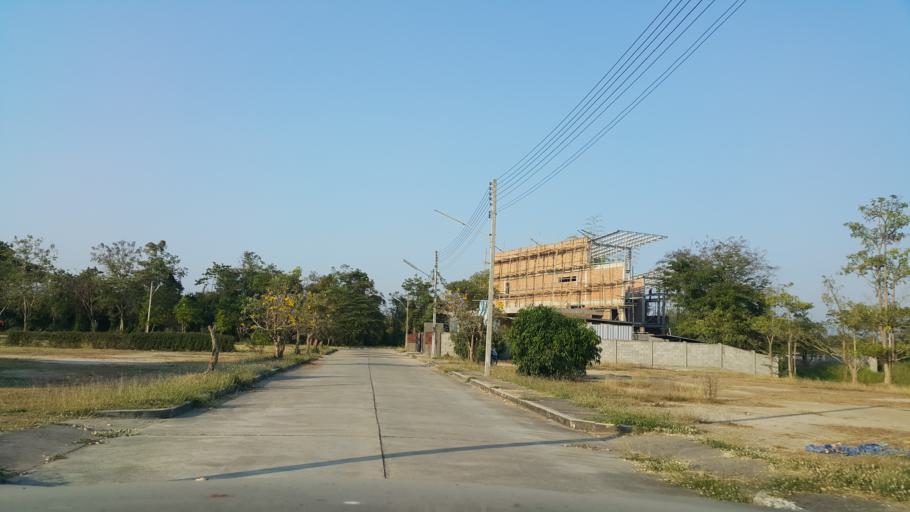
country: TH
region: Chiang Mai
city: San Sai
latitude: 18.8392
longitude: 99.0970
